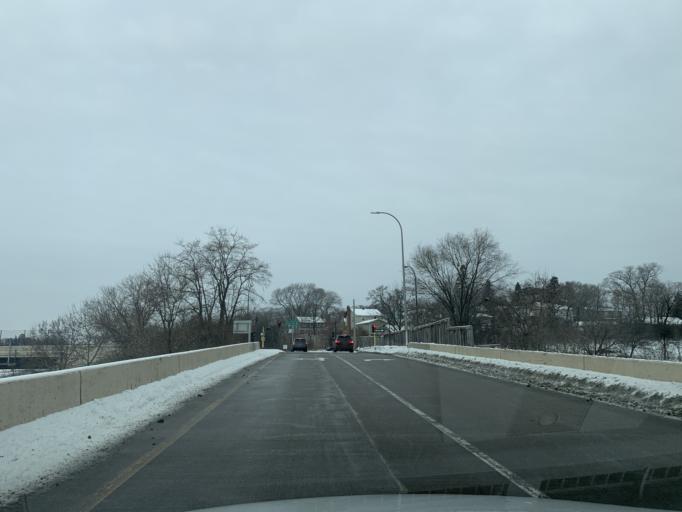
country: US
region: Minnesota
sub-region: Hennepin County
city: Minneapolis
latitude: 44.9703
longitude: -93.3078
